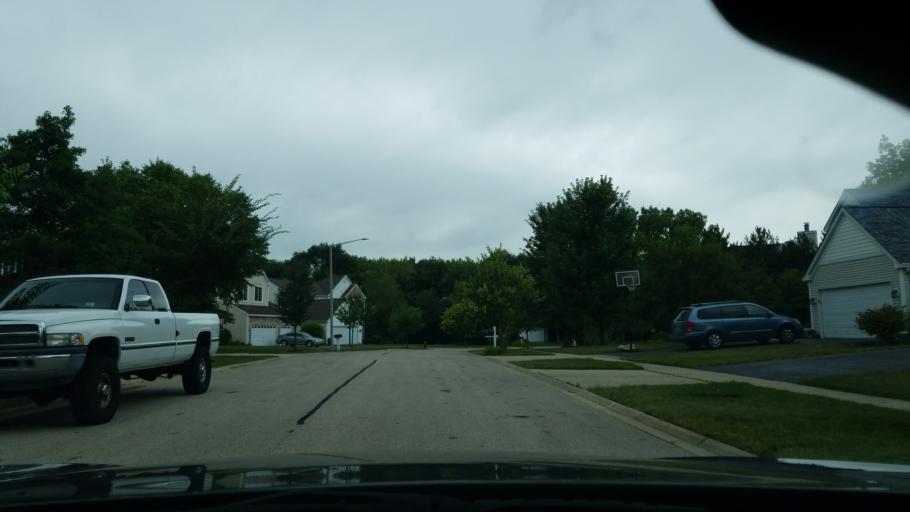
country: US
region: Illinois
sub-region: McHenry County
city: Lake in the Hills
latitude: 42.1694
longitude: -88.3208
